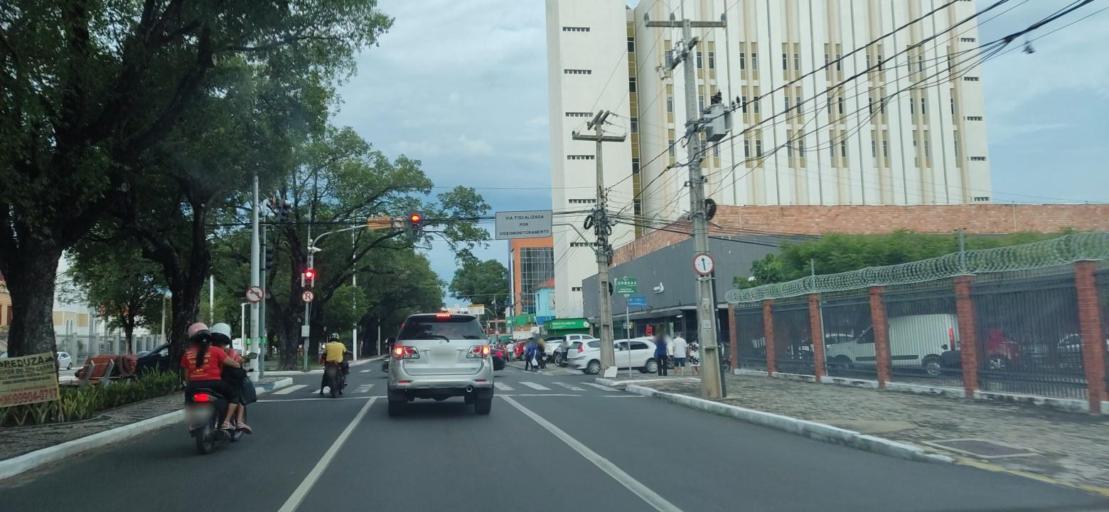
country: BR
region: Piaui
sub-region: Teresina
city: Teresina
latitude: -5.0898
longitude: -42.8097
